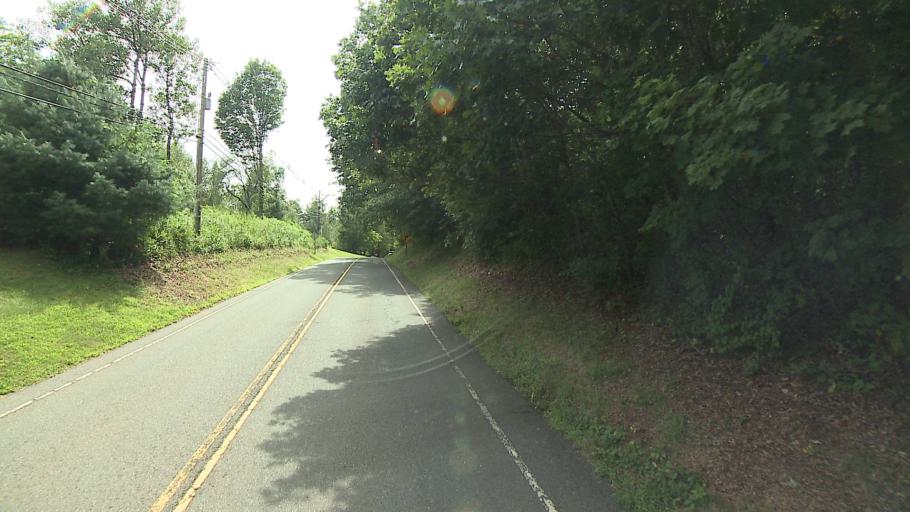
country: US
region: Connecticut
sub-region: Litchfield County
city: Bethlehem Village
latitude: 41.6247
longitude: -73.2266
